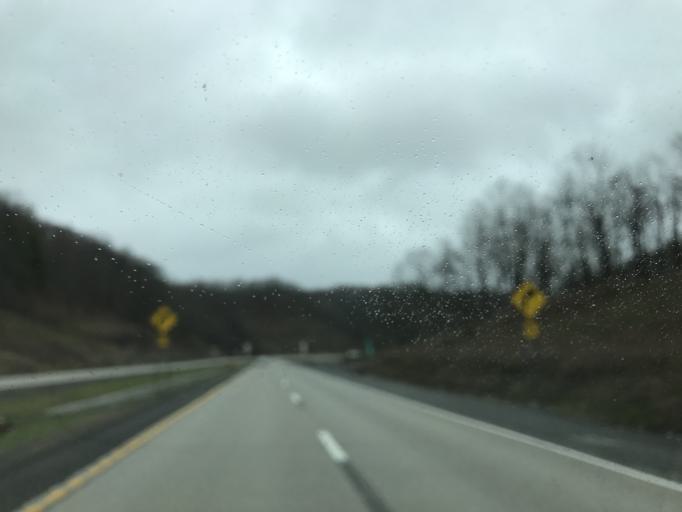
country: US
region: West Virginia
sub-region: Summers County
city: Hinton
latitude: 37.7803
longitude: -80.9705
